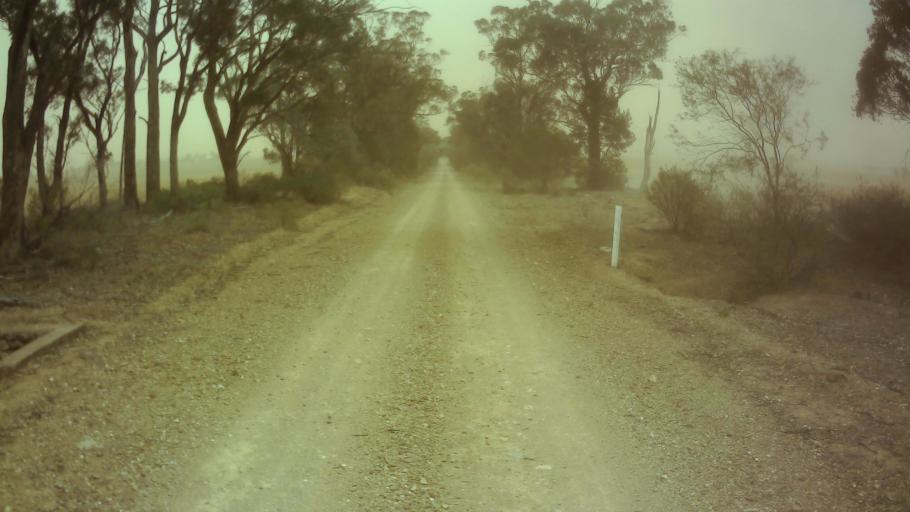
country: AU
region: New South Wales
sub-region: Weddin
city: Grenfell
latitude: -33.7085
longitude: 147.9430
